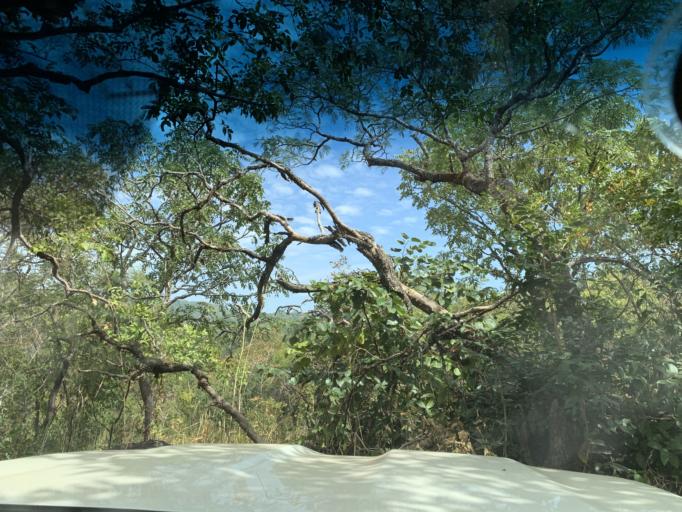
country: GN
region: Mamou
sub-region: Pita
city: Pita
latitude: 10.9972
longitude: -12.4903
